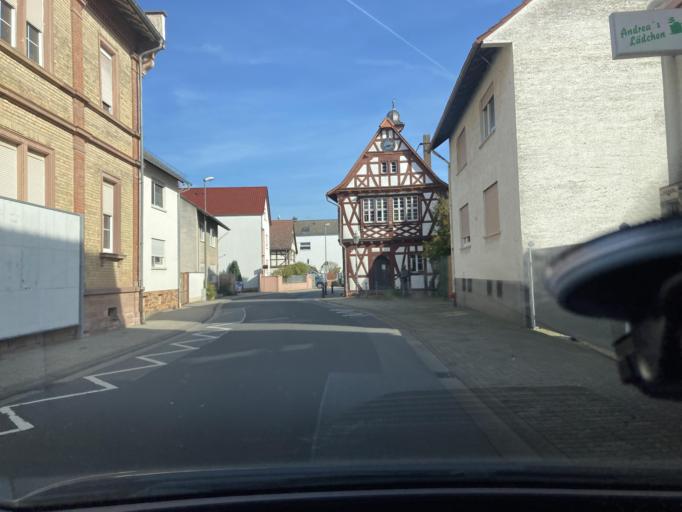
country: DE
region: Hesse
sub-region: Regierungsbezirk Darmstadt
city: Gross-Gerau
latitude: 49.8996
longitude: 8.4829
